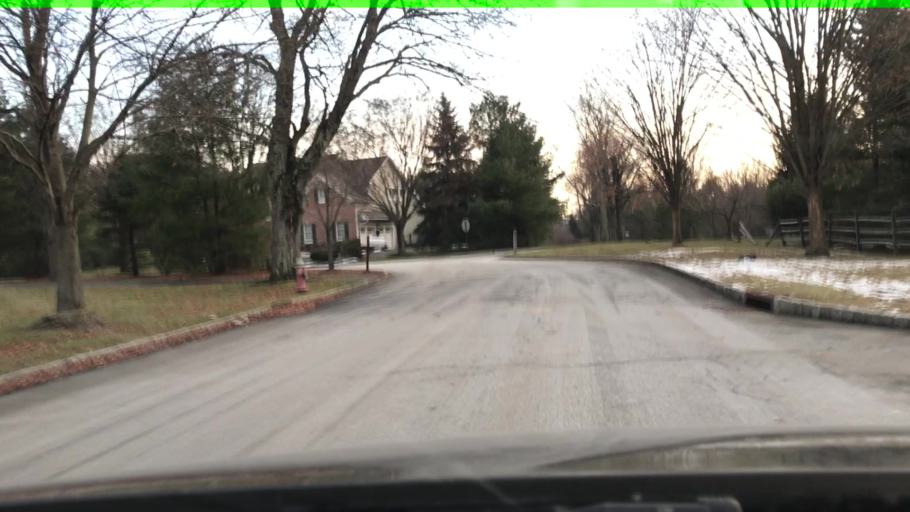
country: US
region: New Jersey
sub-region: Morris County
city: Mendham
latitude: 40.7850
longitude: -74.5837
